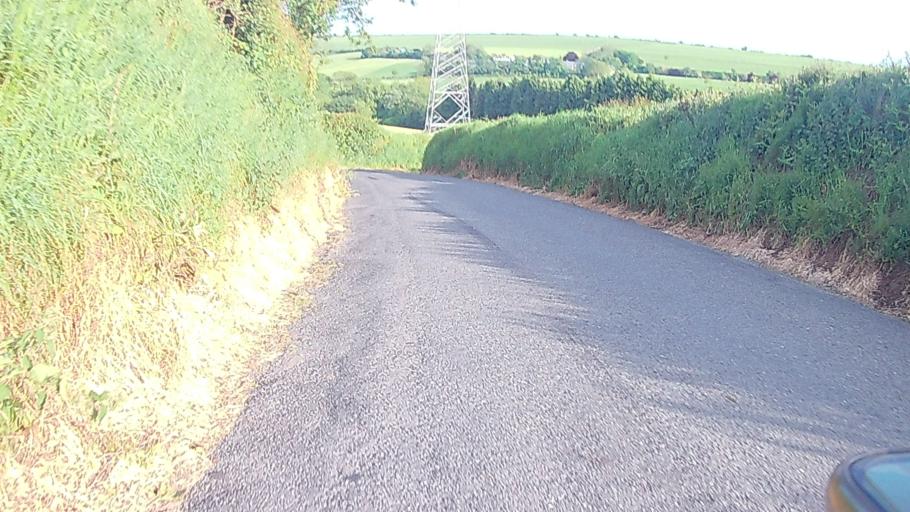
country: IE
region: Munster
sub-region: County Cork
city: Cork
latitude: 51.9772
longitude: -8.4616
